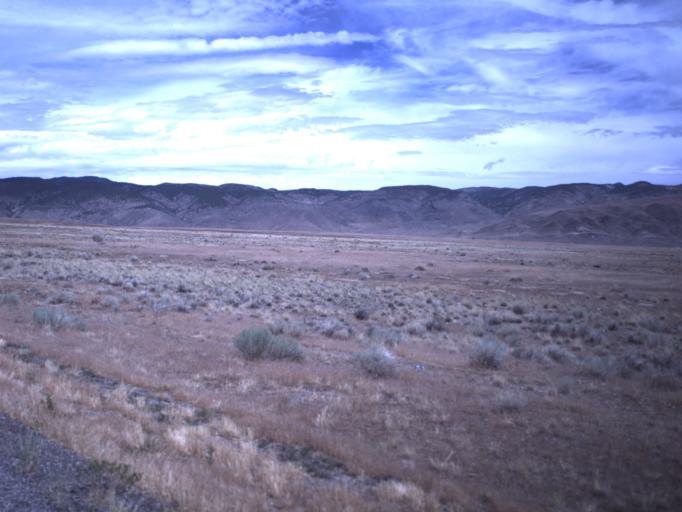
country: US
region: Utah
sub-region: Sevier County
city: Monroe
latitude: 38.6298
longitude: -112.1657
